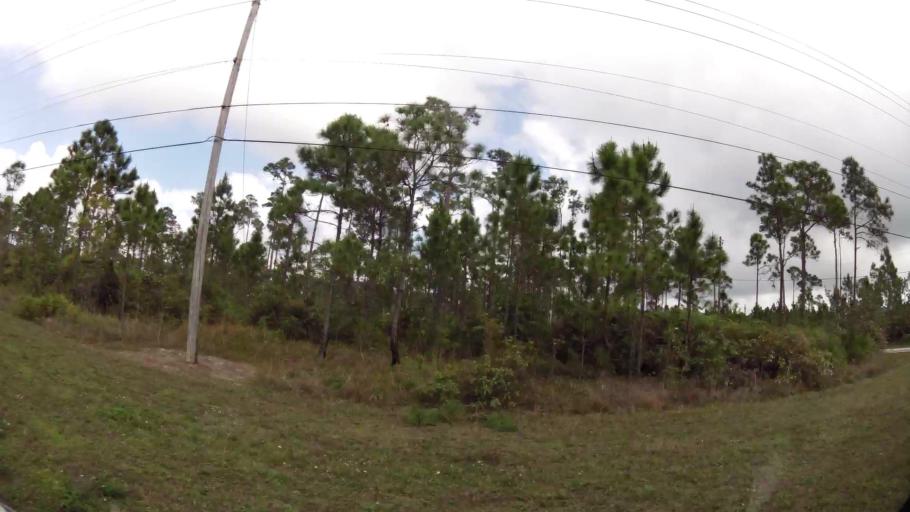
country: BS
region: Freeport
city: Lucaya
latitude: 26.5496
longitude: -78.5802
